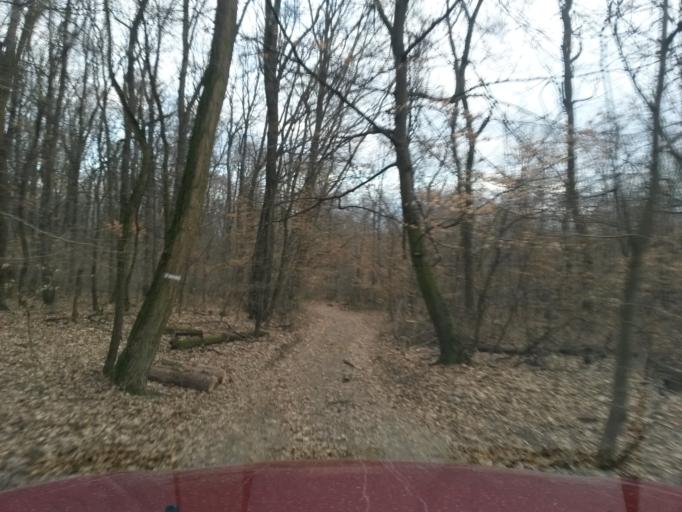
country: SK
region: Kosicky
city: Kosice
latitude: 48.6965
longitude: 21.2984
